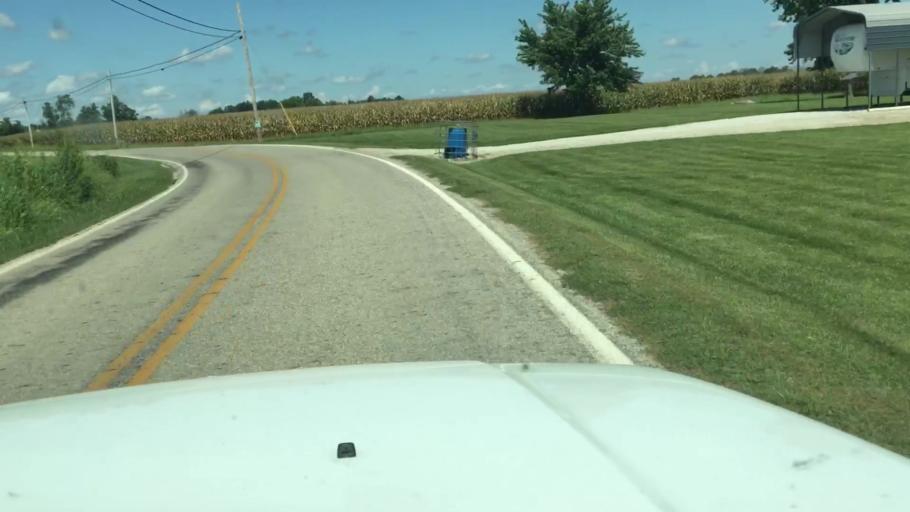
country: US
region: Ohio
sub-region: Madison County
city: Mount Sterling
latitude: 39.6784
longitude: -83.2350
